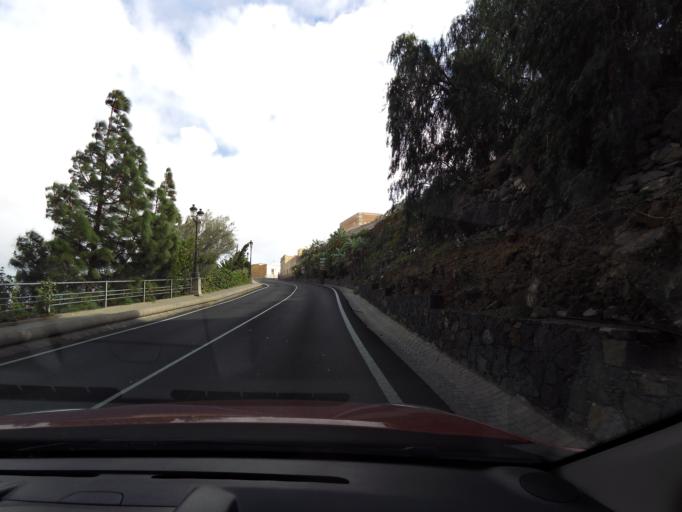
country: ES
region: Canary Islands
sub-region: Provincia de Las Palmas
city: Aguimes
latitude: 27.9077
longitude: -15.4445
